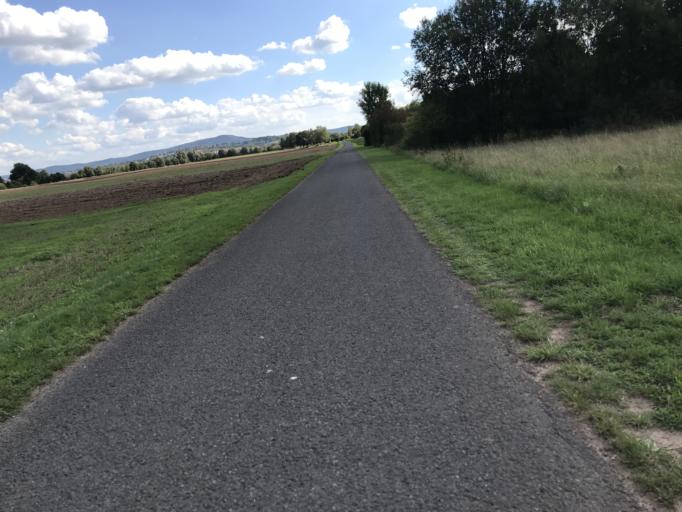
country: DE
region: Hesse
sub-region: Regierungsbezirk Kassel
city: Bad Sooden-Allendorf
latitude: 51.2152
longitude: 9.9962
